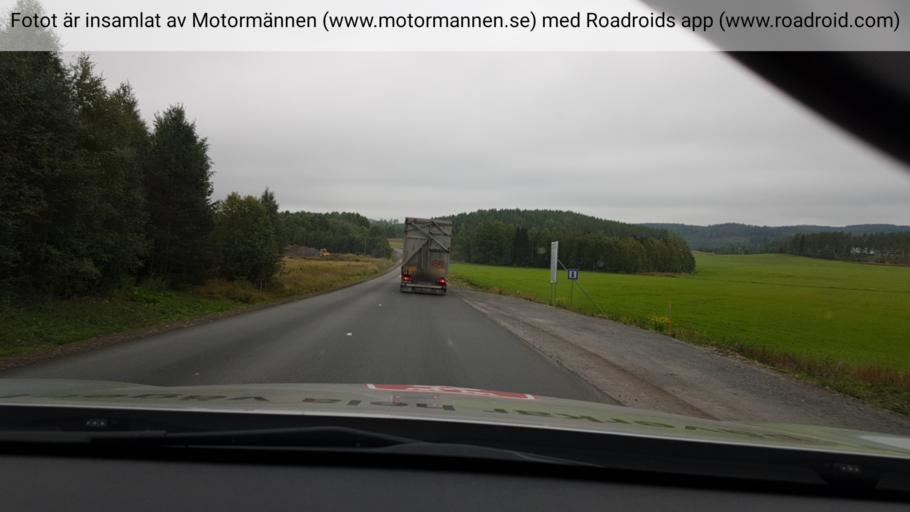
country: SE
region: Vaesterbotten
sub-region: Skelleftea Kommun
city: Burtraesk
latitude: 64.3700
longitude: 20.5030
